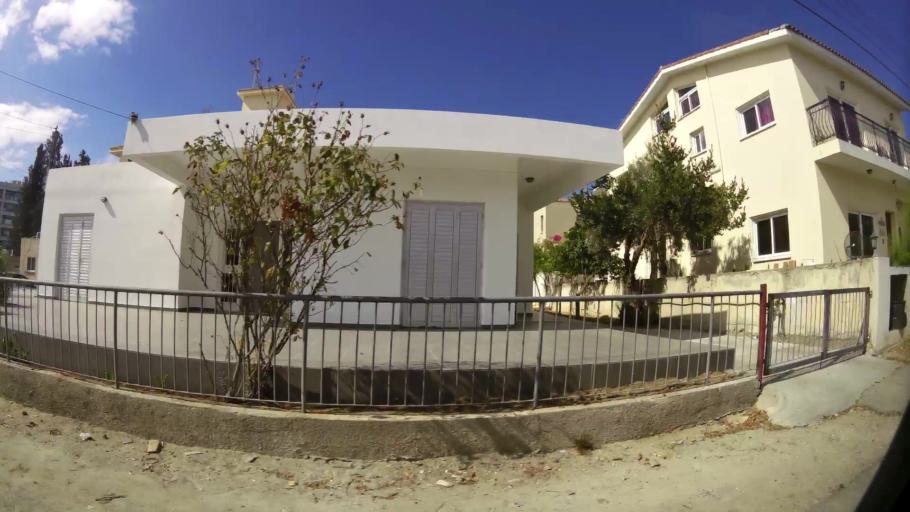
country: CY
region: Lefkosia
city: Nicosia
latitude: 35.1428
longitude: 33.3718
